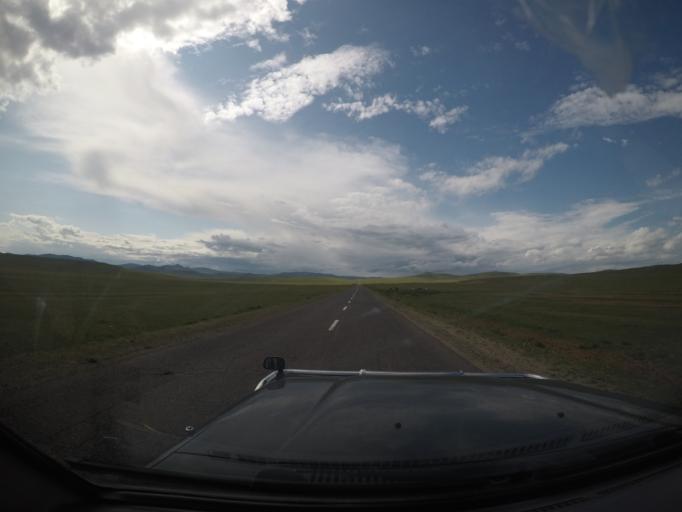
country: MN
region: Hentiy
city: Modot
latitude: 47.5969
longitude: 109.2461
